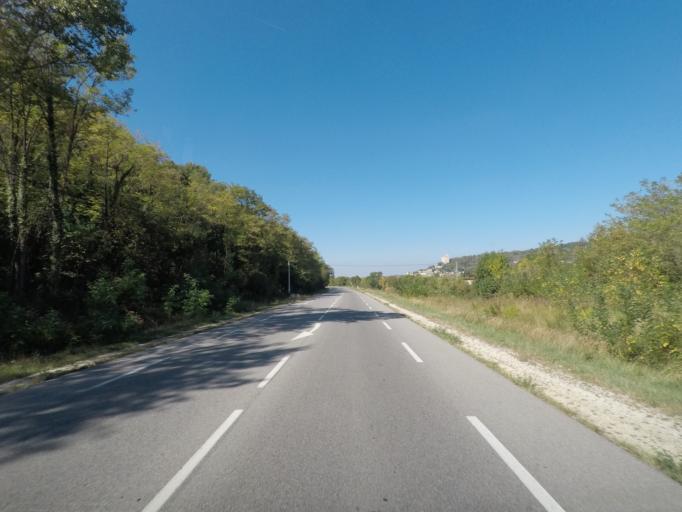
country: FR
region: Rhone-Alpes
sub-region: Departement de la Drome
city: Crest
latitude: 44.7187
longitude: 5.0348
